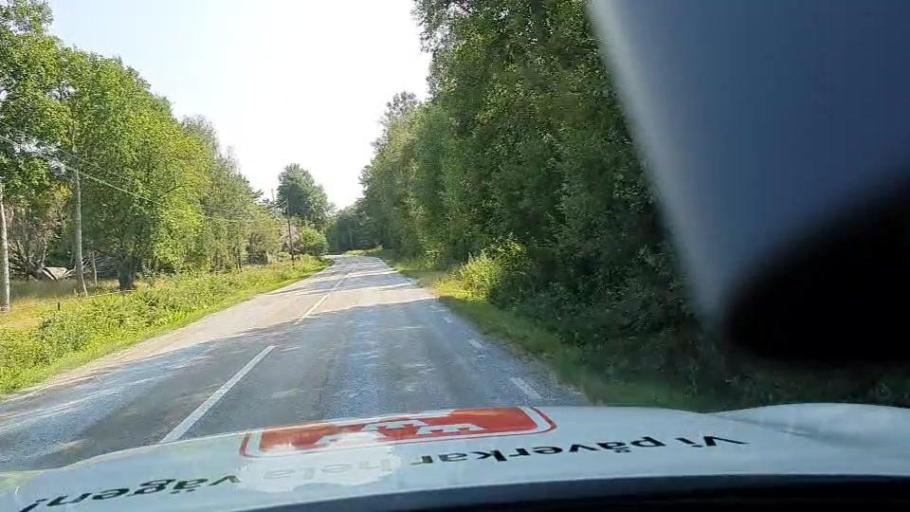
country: SE
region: Vaestra Goetaland
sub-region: Tjorns Kommun
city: Skaerhamn
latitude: 58.1027
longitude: 11.4856
